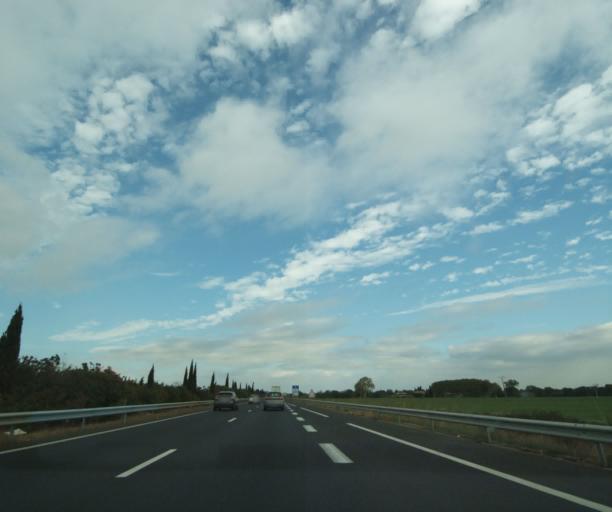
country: FR
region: Provence-Alpes-Cote d'Azur
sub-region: Departement des Bouches-du-Rhone
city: Saint-Martin-de-Crau
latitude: 43.6382
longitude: 4.8633
